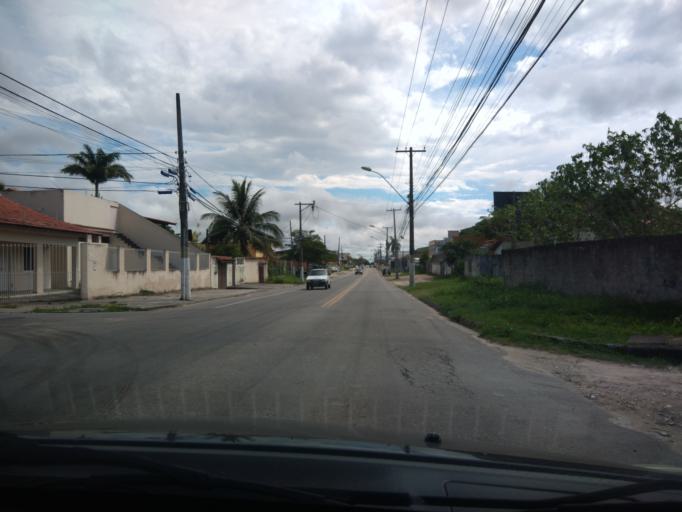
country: BR
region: Rio de Janeiro
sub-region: Niteroi
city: Niteroi
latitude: -22.9259
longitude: -43.0099
